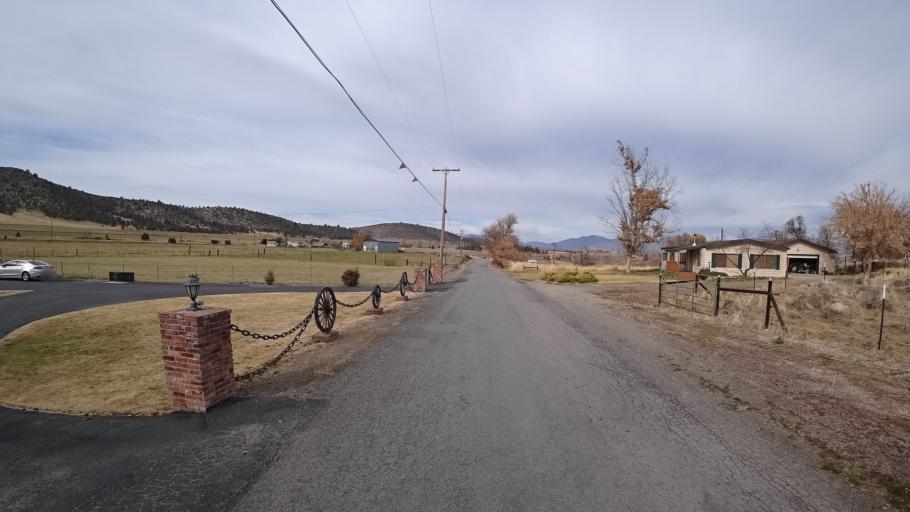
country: US
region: California
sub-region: Siskiyou County
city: Montague
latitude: 41.6824
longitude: -122.5268
